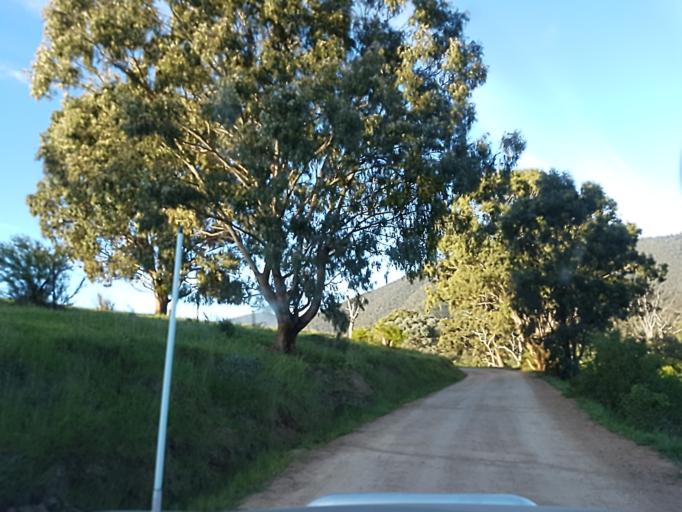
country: AU
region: Victoria
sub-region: East Gippsland
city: Bairnsdale
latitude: -37.4029
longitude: 147.1033
